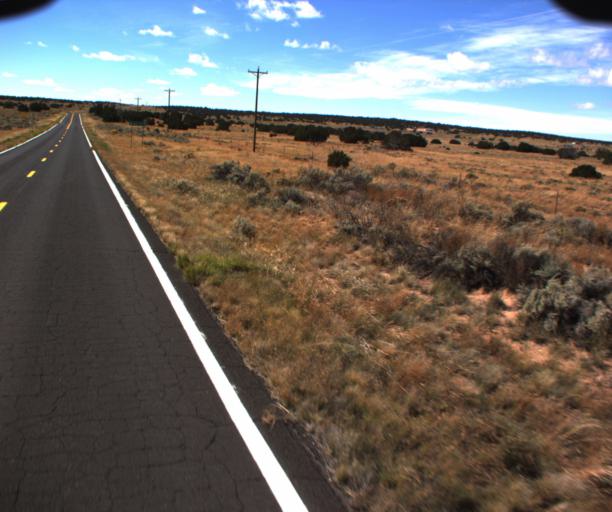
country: US
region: New Mexico
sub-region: McKinley County
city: Zuni Pueblo
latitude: 34.9791
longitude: -109.1300
